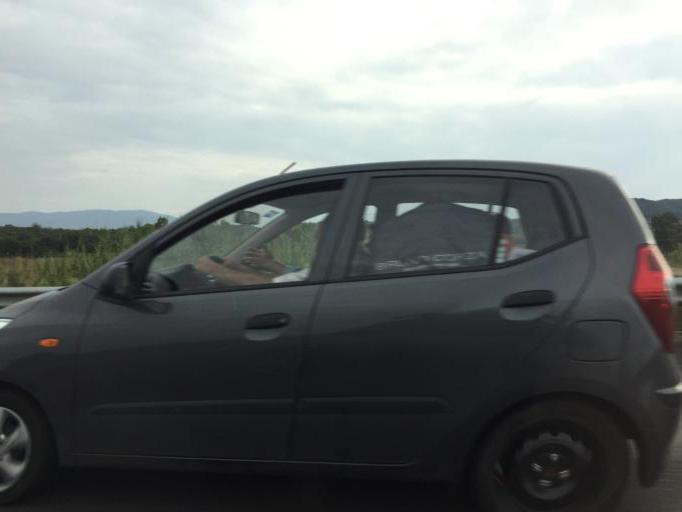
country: MX
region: Michoacan
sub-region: Puruandiro
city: San Lorenzo
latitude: 19.9548
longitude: -101.6572
